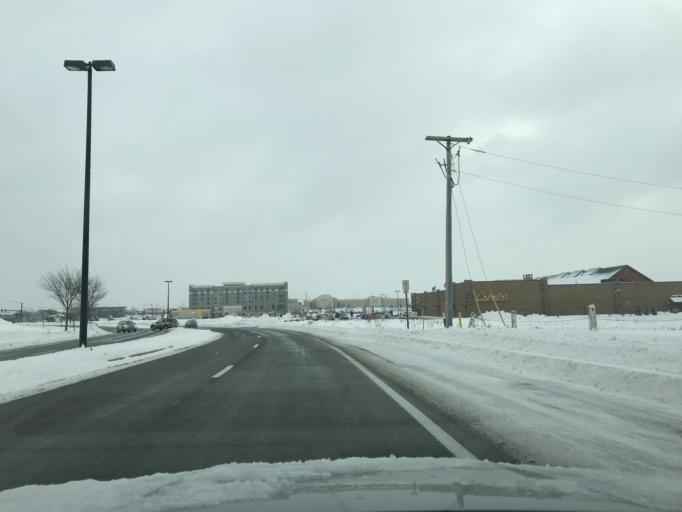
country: US
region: Wisconsin
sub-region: Dane County
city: Sun Prairie
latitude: 43.1649
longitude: -89.2755
